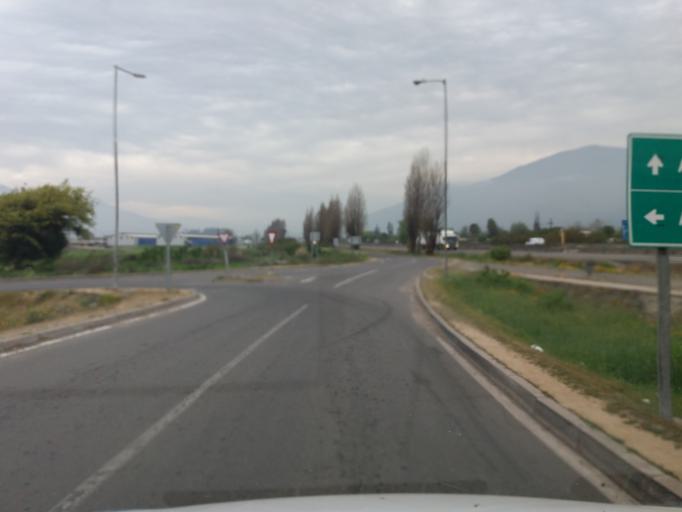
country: CL
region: Valparaiso
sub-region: Provincia de Quillota
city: Hacienda La Calera
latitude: -32.8455
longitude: -71.1005
